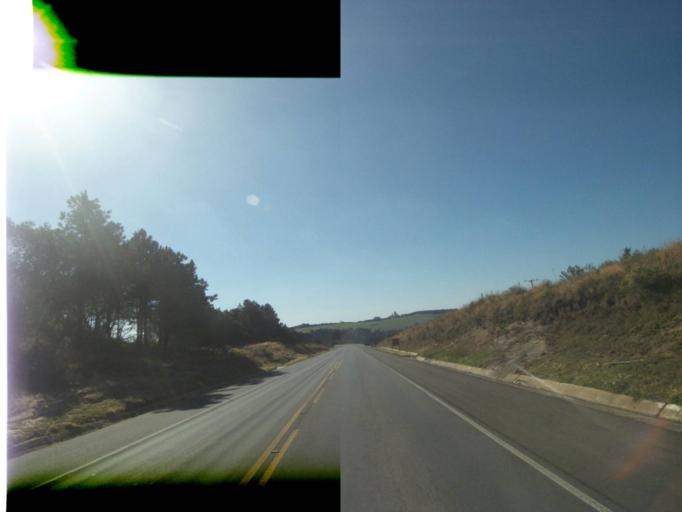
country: BR
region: Parana
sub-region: Tibagi
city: Tibagi
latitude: -24.7969
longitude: -50.4668
